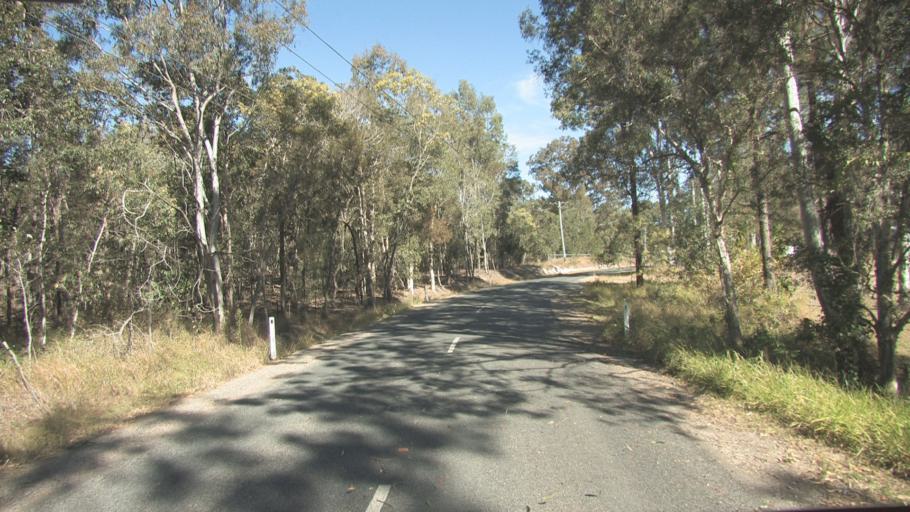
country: AU
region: Queensland
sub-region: Ipswich
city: Springfield Lakes
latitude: -27.7169
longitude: 152.9393
